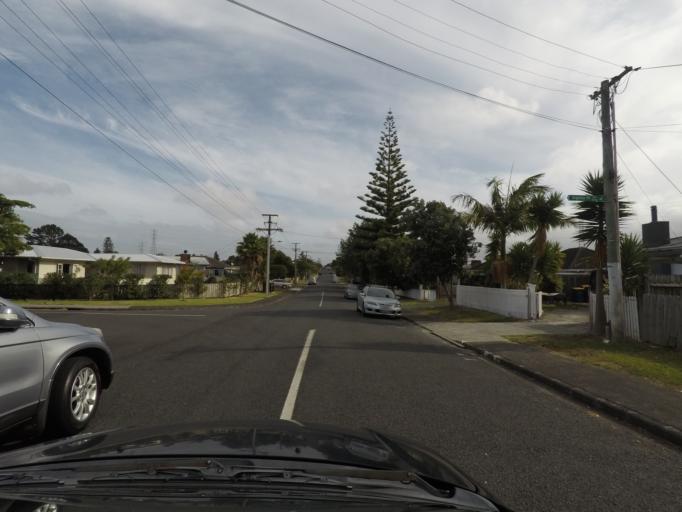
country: NZ
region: Auckland
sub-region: Auckland
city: Rosebank
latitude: -36.8915
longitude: 174.6680
